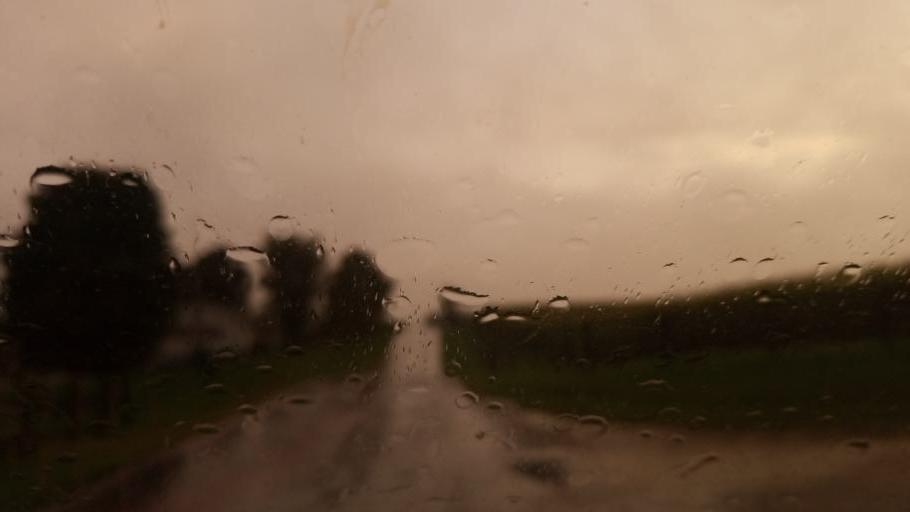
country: US
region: Kentucky
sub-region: Fleming County
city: Flemingsburg
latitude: 38.4593
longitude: -83.6427
